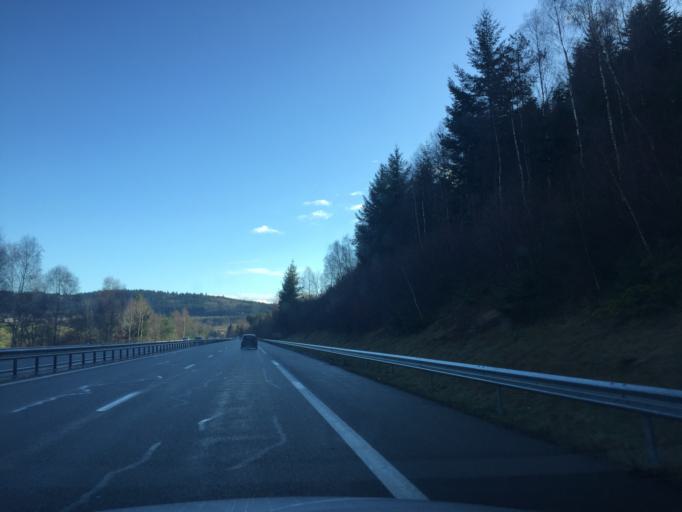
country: FR
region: Rhone-Alpes
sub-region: Departement de la Loire
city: Noiretable
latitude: 45.8485
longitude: 3.7320
